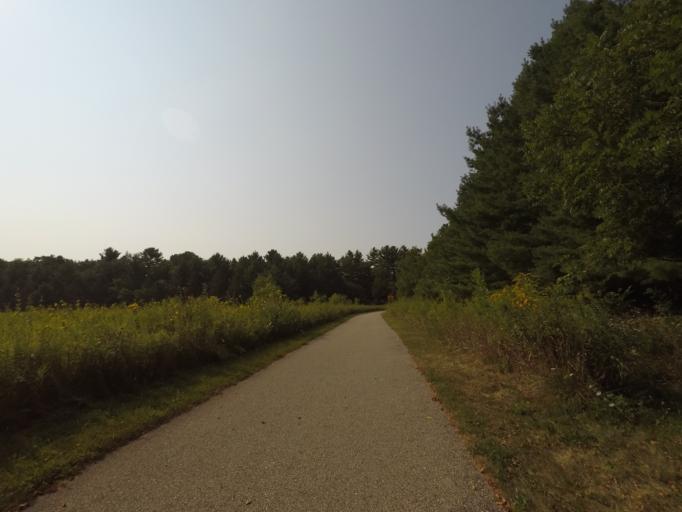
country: US
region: Wisconsin
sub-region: Waukesha County
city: Delafield
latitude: 43.0372
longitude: -88.4139
